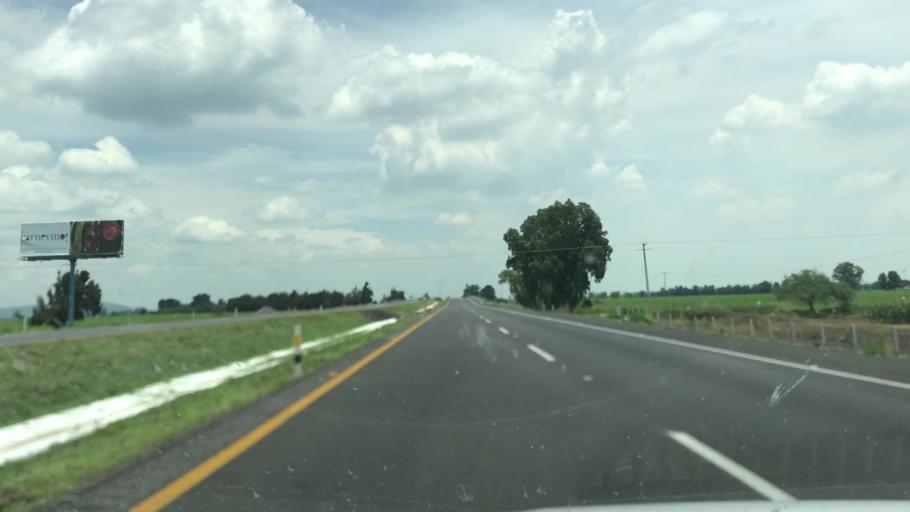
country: MX
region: Guanajuato
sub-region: Salamanca
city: San Vicente de Flores
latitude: 20.6326
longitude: -101.2533
